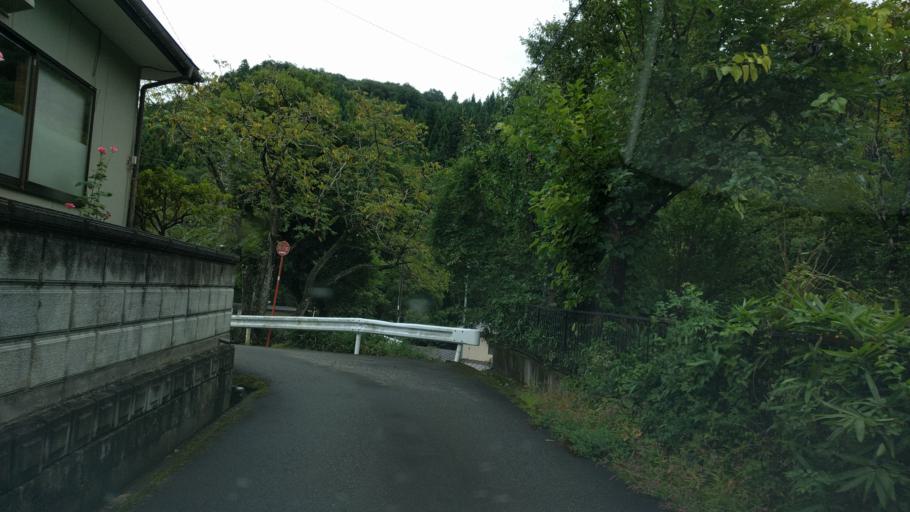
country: JP
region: Fukushima
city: Kitakata
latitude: 37.5066
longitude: 139.9568
